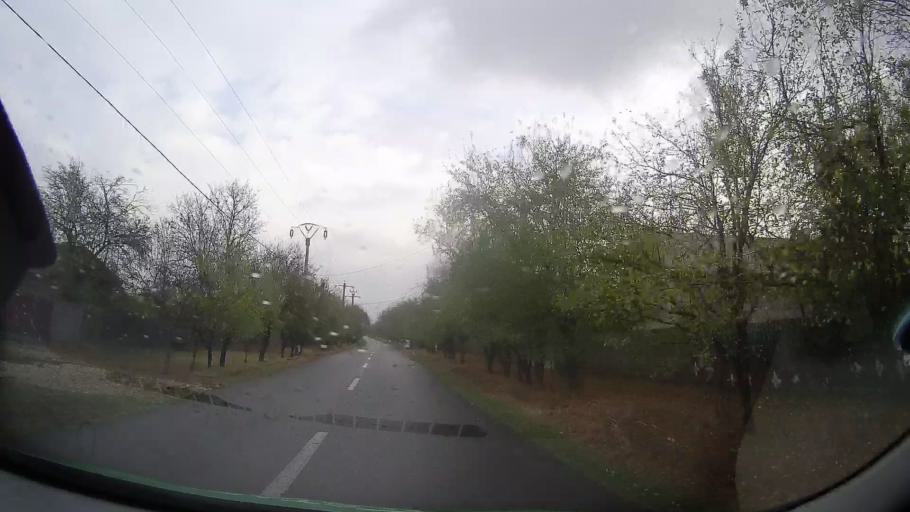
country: RO
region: Ialomita
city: Brazii
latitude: 44.7783
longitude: 26.3352
